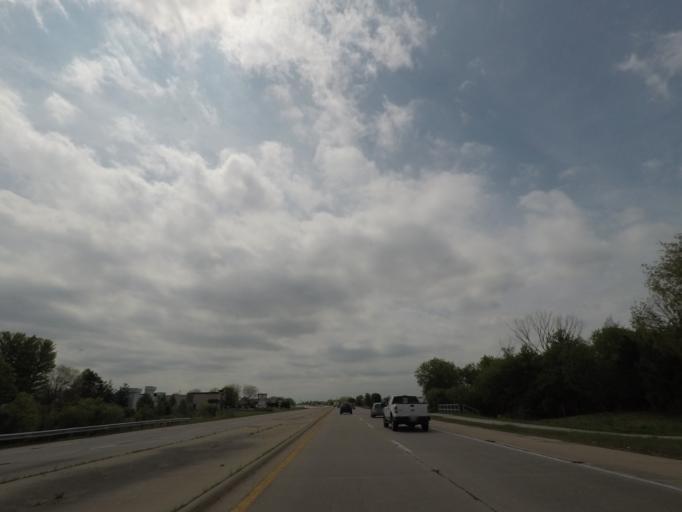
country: US
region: Illinois
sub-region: Winnebago County
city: Cherry Valley
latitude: 42.3013
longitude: -88.9796
